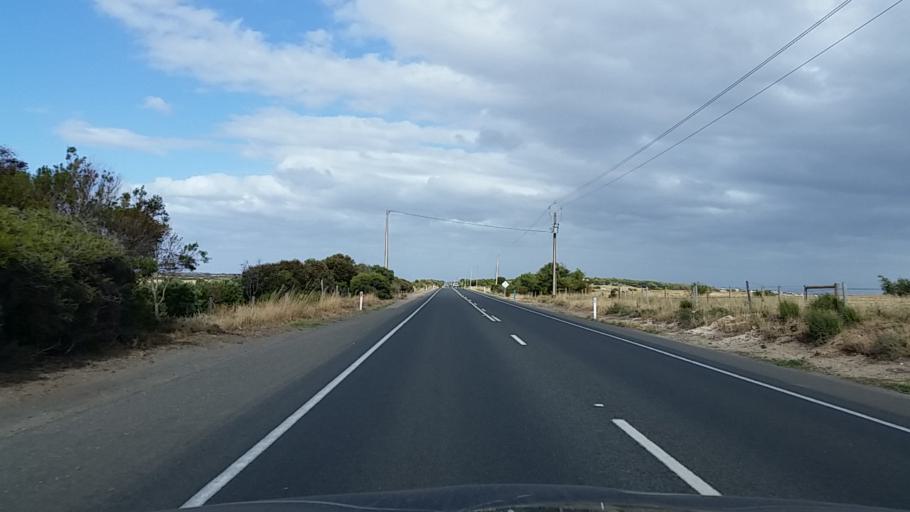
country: AU
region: South Australia
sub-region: Alexandrina
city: Goolwa
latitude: -35.5084
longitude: 138.7360
